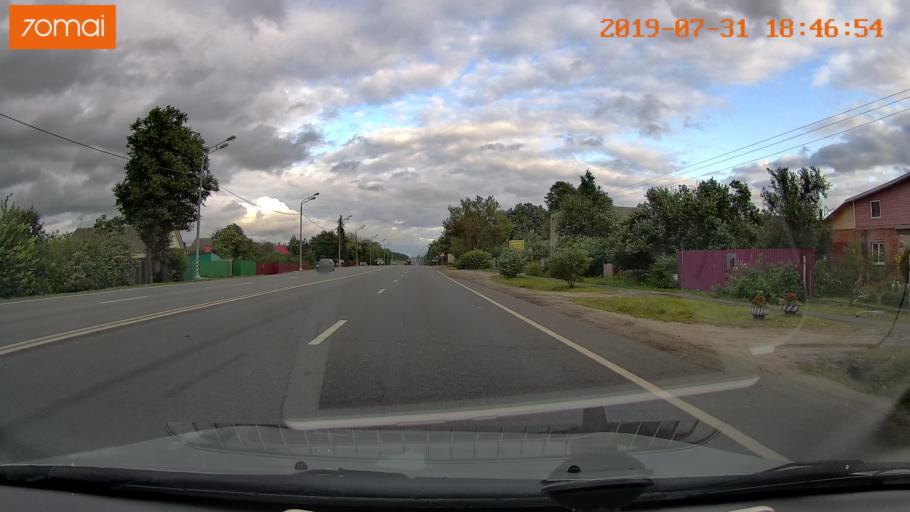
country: RU
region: Moskovskaya
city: Troitskoye
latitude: 55.2431
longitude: 38.5352
